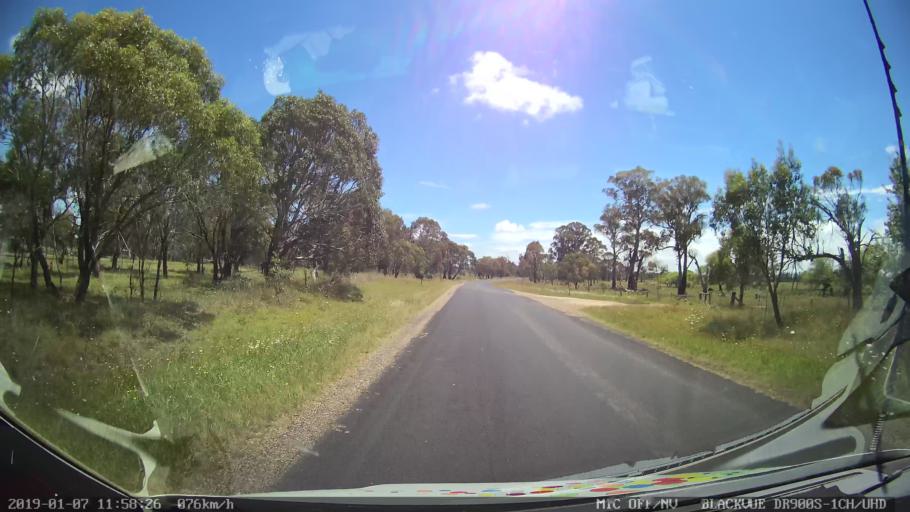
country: AU
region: New South Wales
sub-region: Guyra
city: Guyra
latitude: -30.2534
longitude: 151.6674
